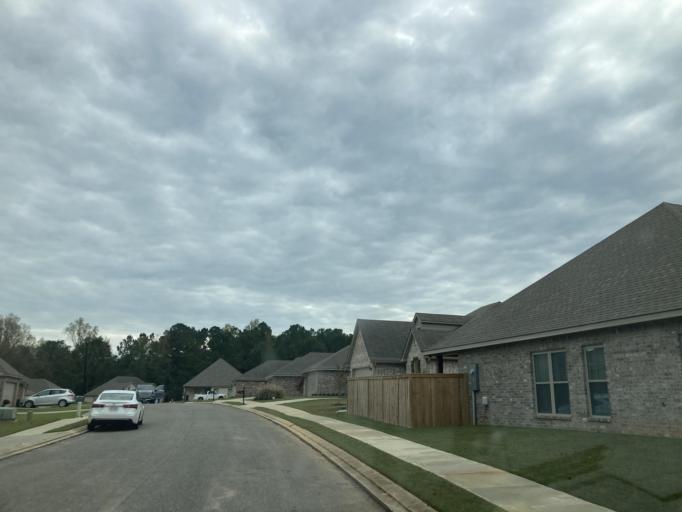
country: US
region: Mississippi
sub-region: Lamar County
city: West Hattiesburg
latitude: 31.2990
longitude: -89.4445
